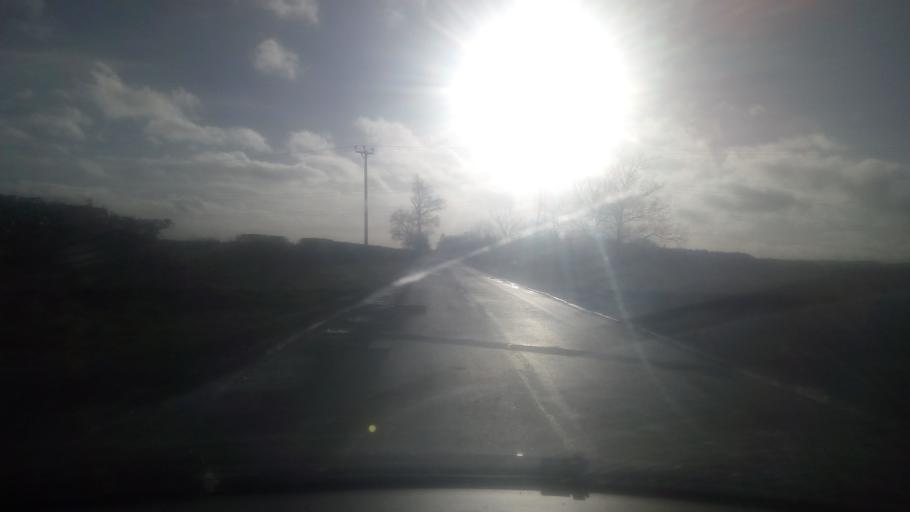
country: GB
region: Scotland
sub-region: The Scottish Borders
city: Coldstream
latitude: 55.6995
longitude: -2.3136
